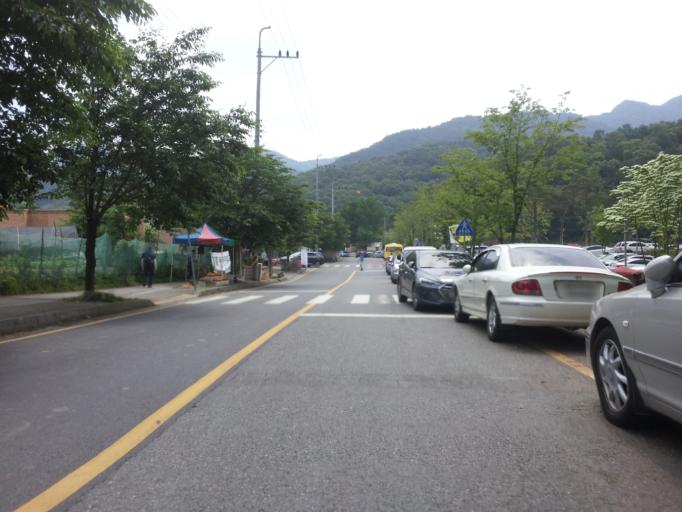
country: KR
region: Daejeon
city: Daejeon
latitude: 36.3305
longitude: 127.4822
